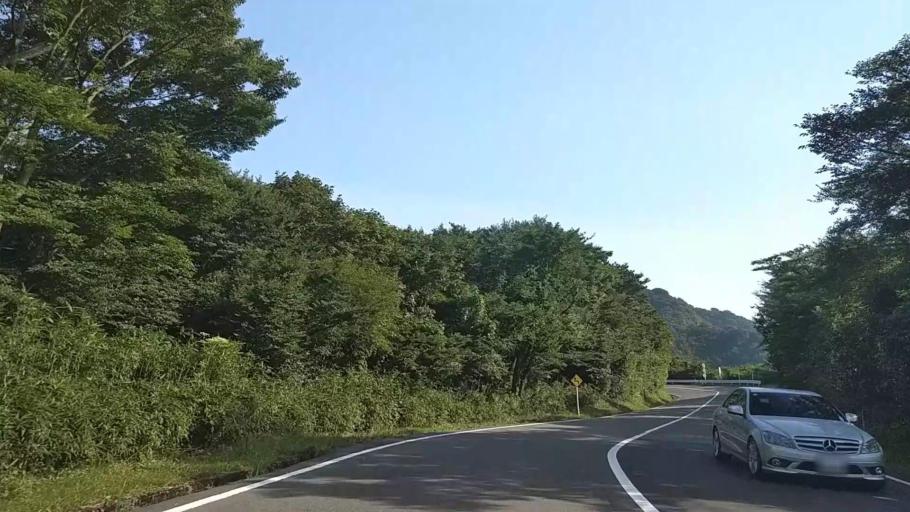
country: JP
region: Kanagawa
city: Hakone
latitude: 35.2248
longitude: 138.9821
